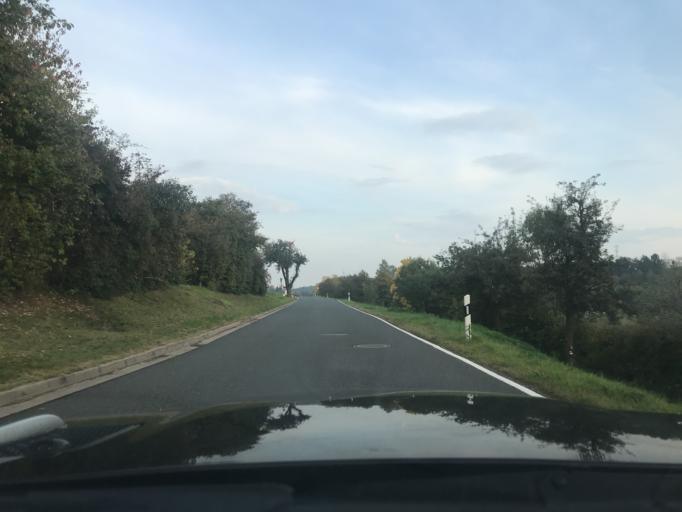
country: DE
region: Thuringia
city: Helmsdorf
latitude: 51.2765
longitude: 10.4104
